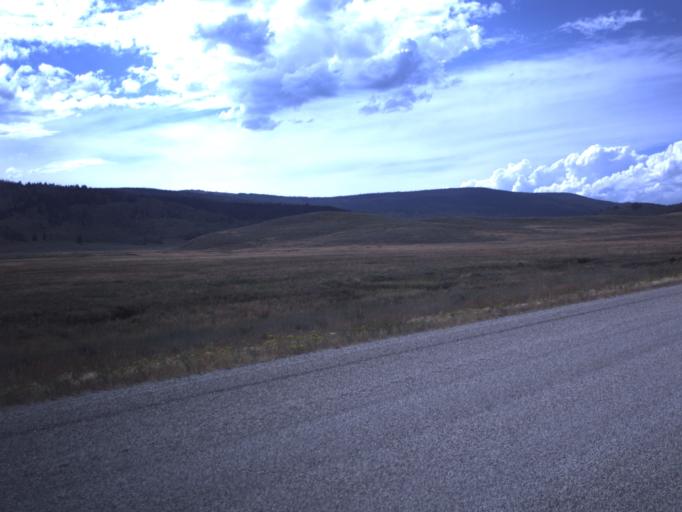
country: US
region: Utah
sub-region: Wasatch County
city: Heber
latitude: 40.2654
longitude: -111.2104
